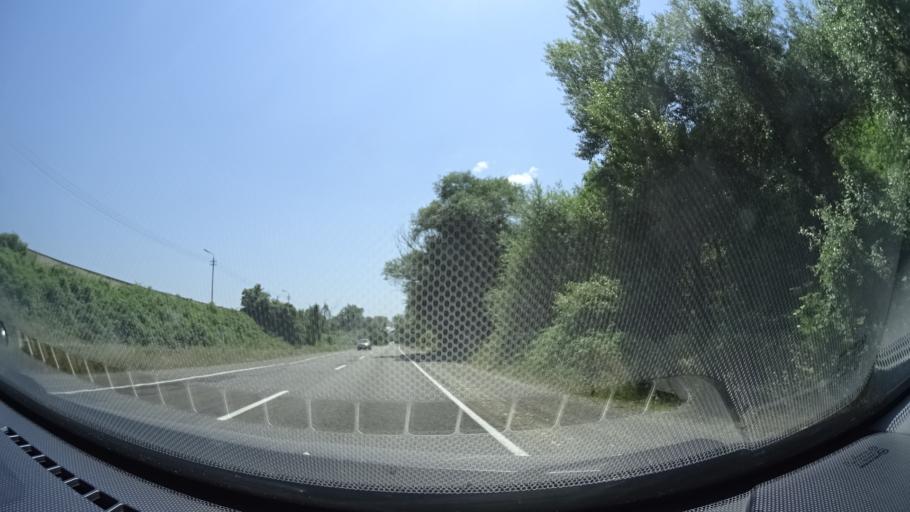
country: GE
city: Zhinvali
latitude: 42.0437
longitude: 44.7453
